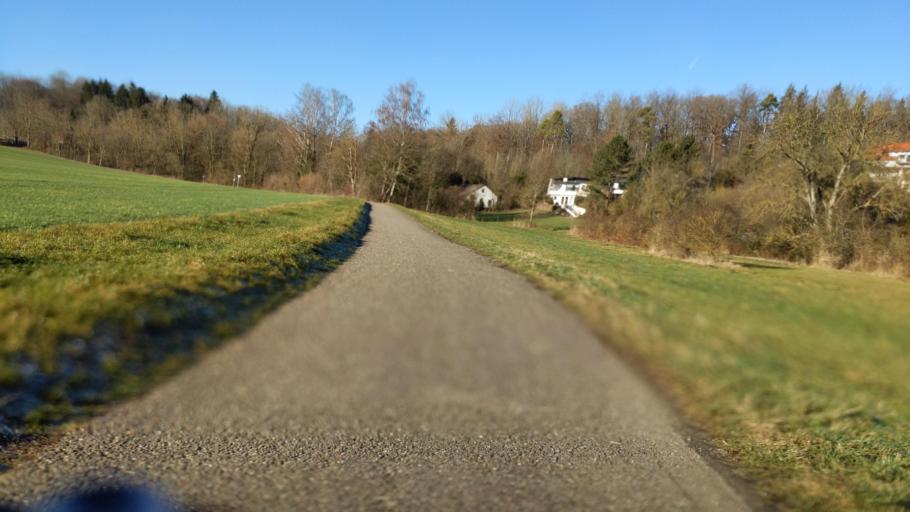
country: DE
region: Baden-Wuerttemberg
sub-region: Regierungsbezirk Stuttgart
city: Rutesheim
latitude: 48.7878
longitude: 8.9597
